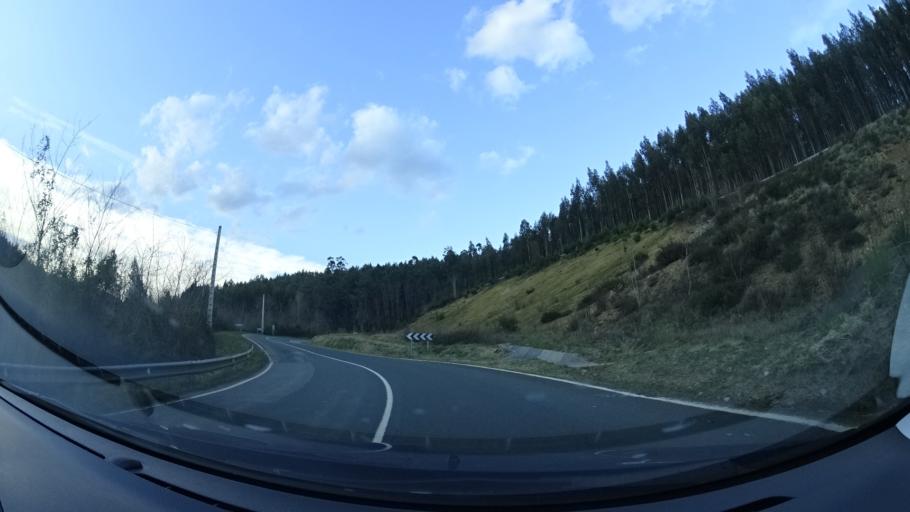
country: ES
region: Basque Country
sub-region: Bizkaia
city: Gatika
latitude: 43.3930
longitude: -2.8956
